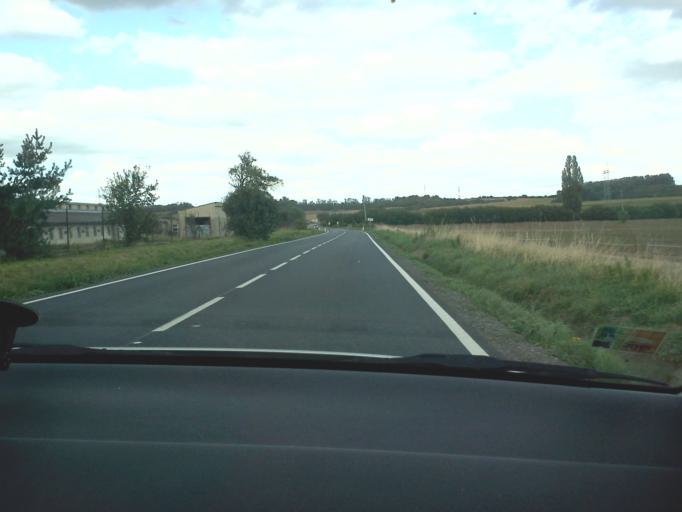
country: CZ
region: Central Bohemia
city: Cesky Brod
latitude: 50.1112
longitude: 14.8605
